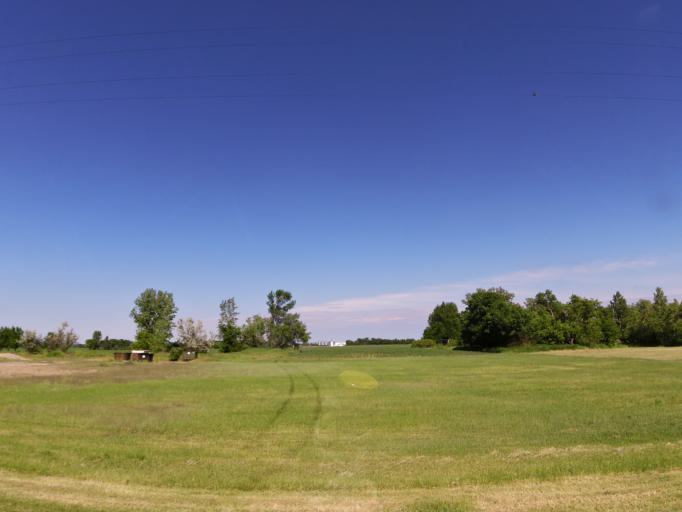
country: US
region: North Dakota
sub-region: Walsh County
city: Grafton
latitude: 48.2966
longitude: -97.2547
